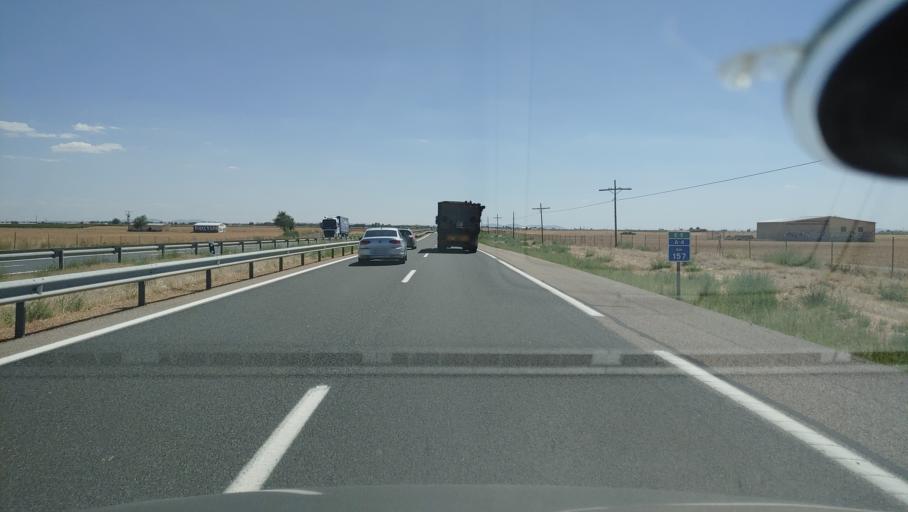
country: ES
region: Castille-La Mancha
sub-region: Provincia de Ciudad Real
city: Villarta de San Juan
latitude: 39.1494
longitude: -3.3865
